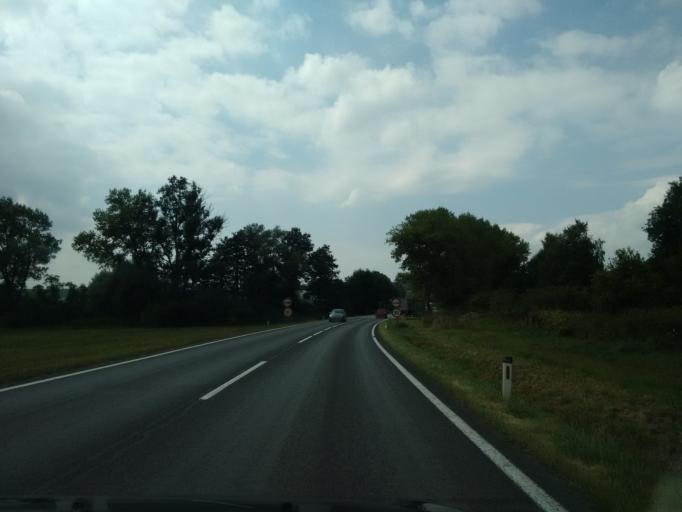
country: AT
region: Upper Austria
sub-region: Politischer Bezirk Grieskirchen
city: Bad Schallerbach
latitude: 48.2209
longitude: 13.9492
